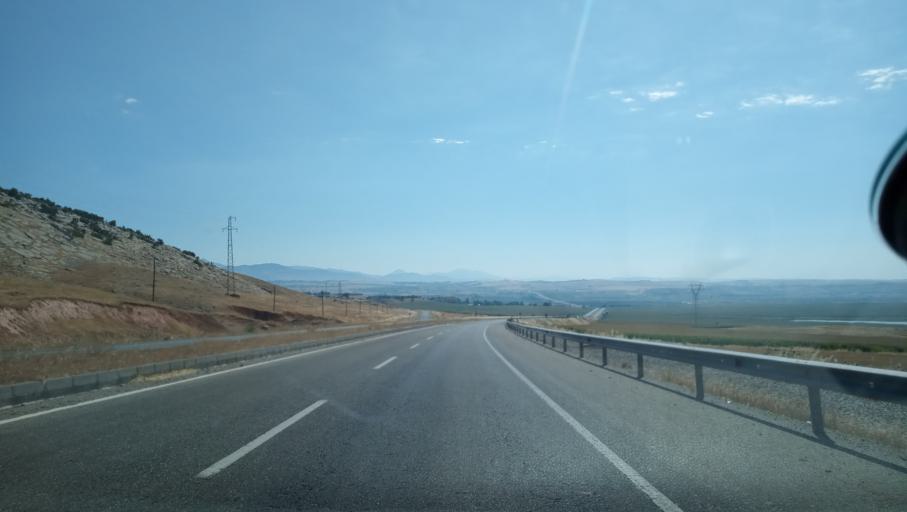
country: TR
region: Diyarbakir
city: Malabadi
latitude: 38.1277
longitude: 41.1713
